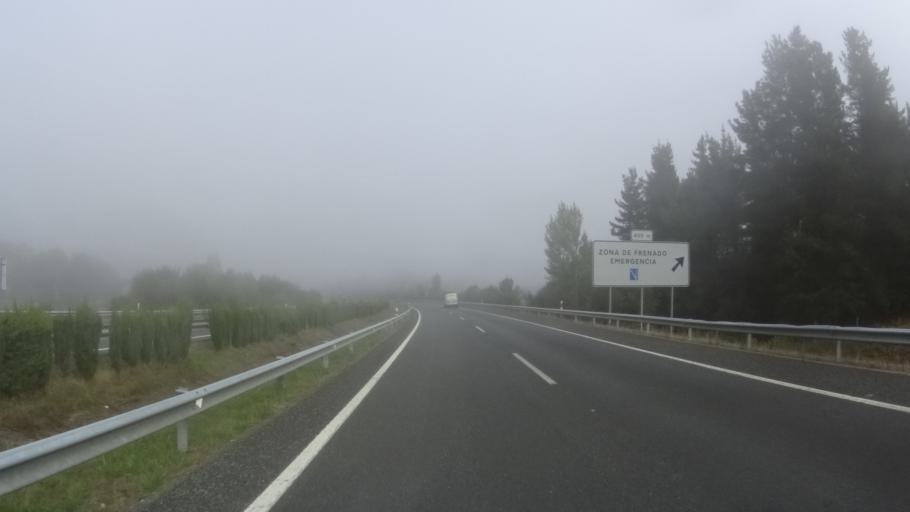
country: ES
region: Galicia
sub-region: Provincia de Lugo
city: O Paramo
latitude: 42.9274
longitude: -7.3590
